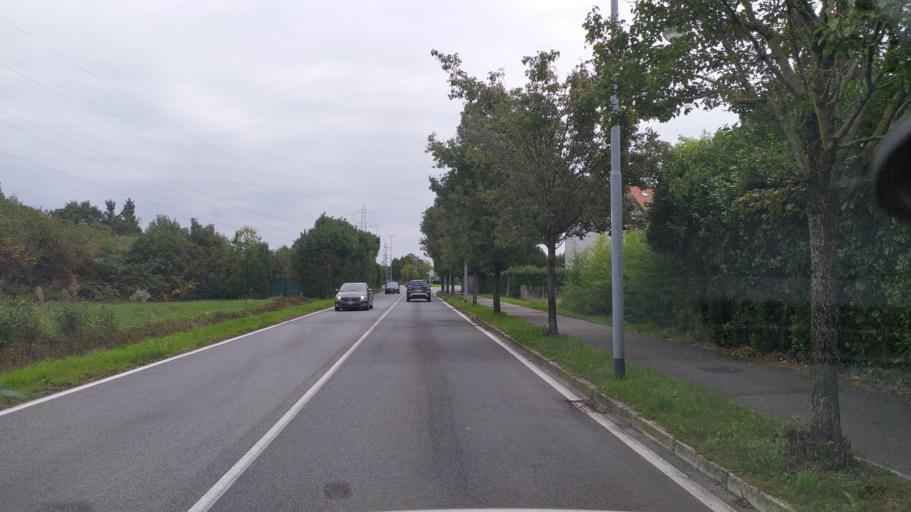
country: IT
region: Lombardy
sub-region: Provincia di Monza e Brianza
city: Desio
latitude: 45.6318
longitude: 9.2023
